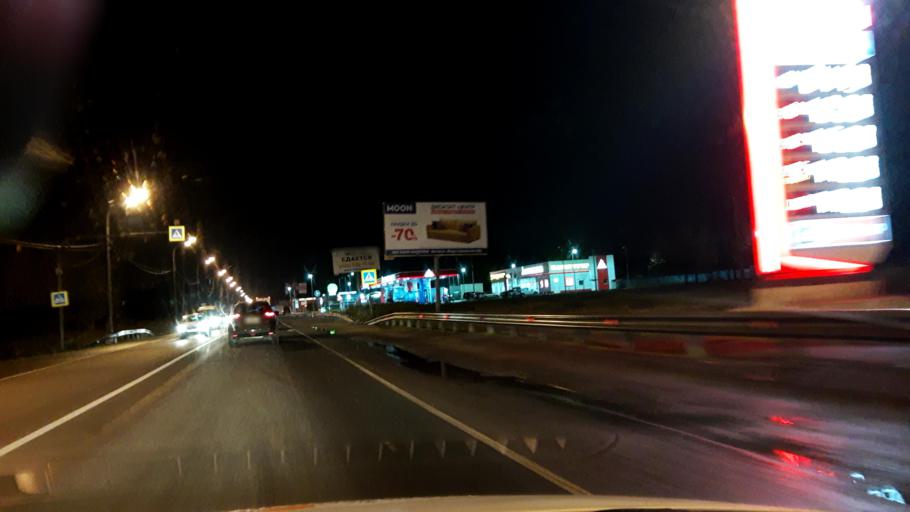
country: RU
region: Moskovskaya
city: Elektrostal'
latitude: 55.8144
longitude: 38.4260
